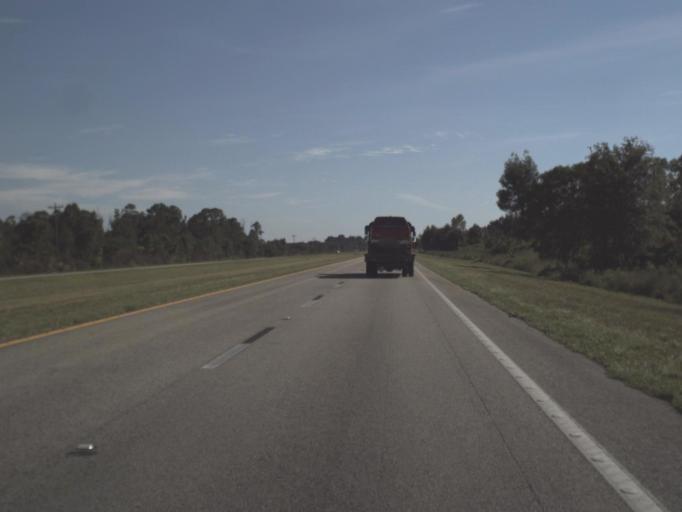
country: US
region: Florida
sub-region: Hendry County
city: Port LaBelle
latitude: 26.9824
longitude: -81.3221
